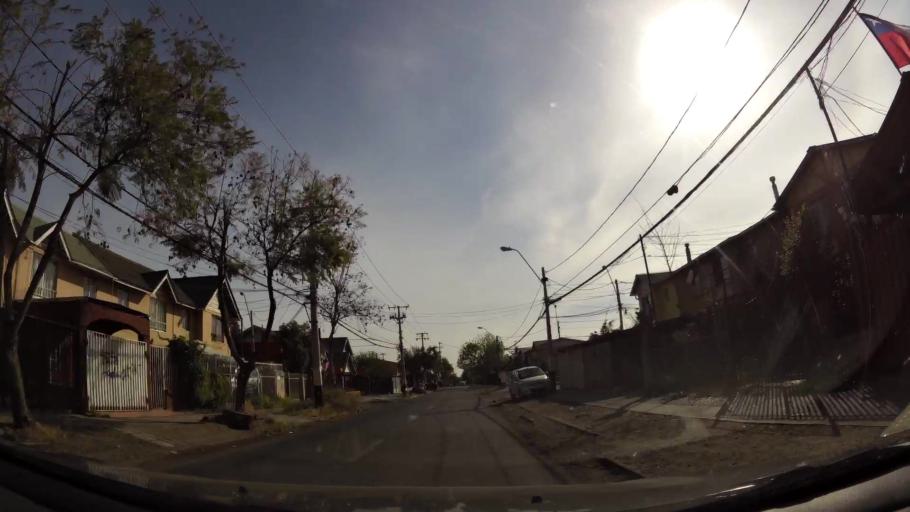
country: CL
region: Santiago Metropolitan
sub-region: Provincia de Cordillera
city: Puente Alto
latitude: -33.5869
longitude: -70.5547
